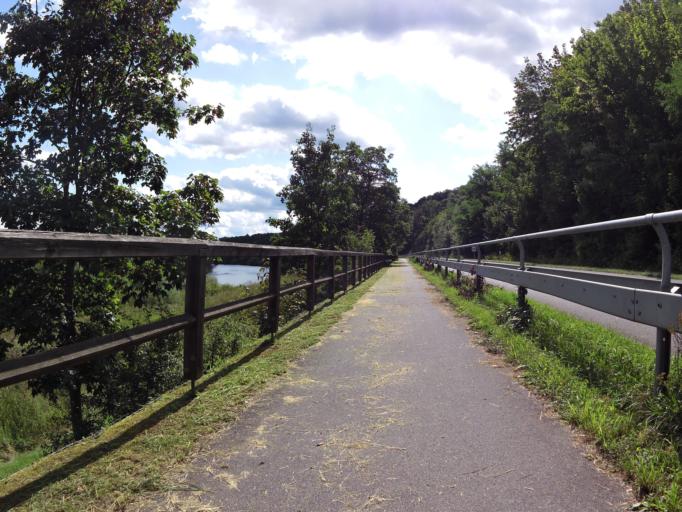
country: DE
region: Bavaria
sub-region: Regierungsbezirk Unterfranken
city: Nordheim
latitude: 49.8554
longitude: 10.2030
